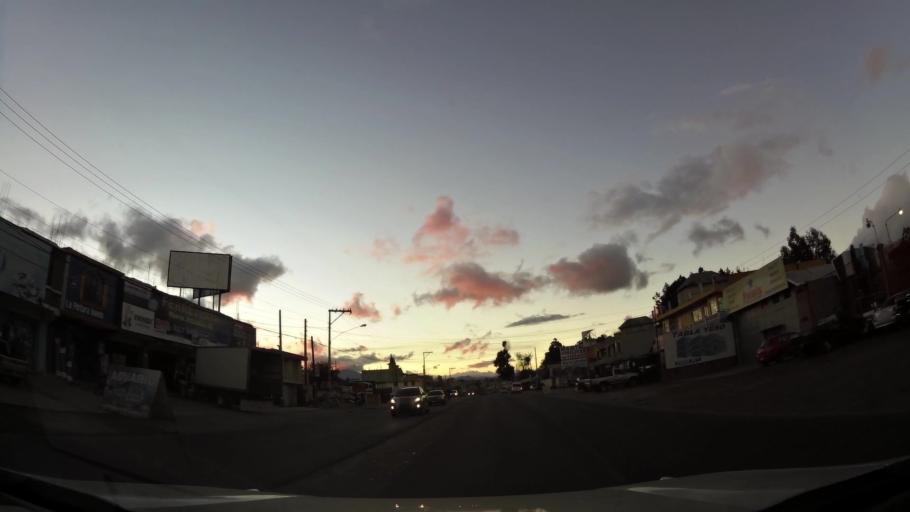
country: GT
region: Quetzaltenango
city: Olintepeque
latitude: 14.8626
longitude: -91.5308
